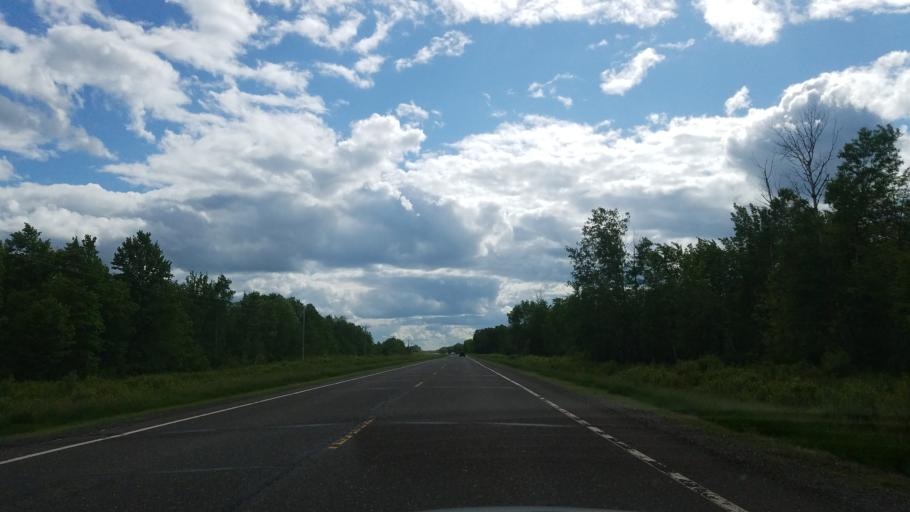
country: US
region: Wisconsin
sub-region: Burnett County
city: Siren
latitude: 46.1926
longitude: -92.1753
